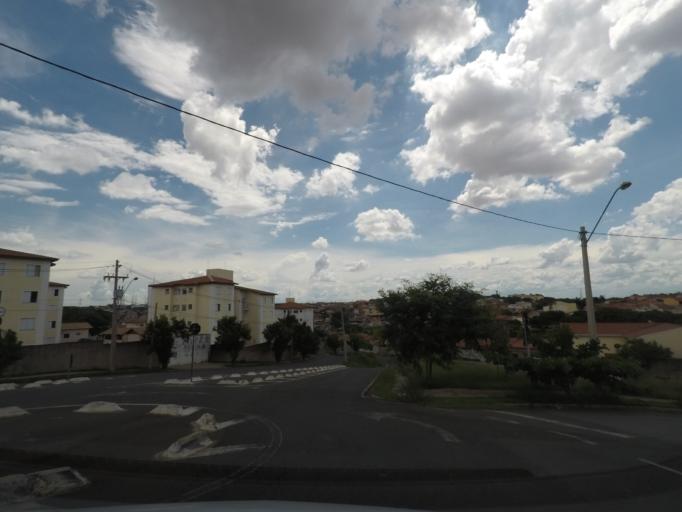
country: BR
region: Sao Paulo
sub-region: Campinas
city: Campinas
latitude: -22.9249
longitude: -47.0179
